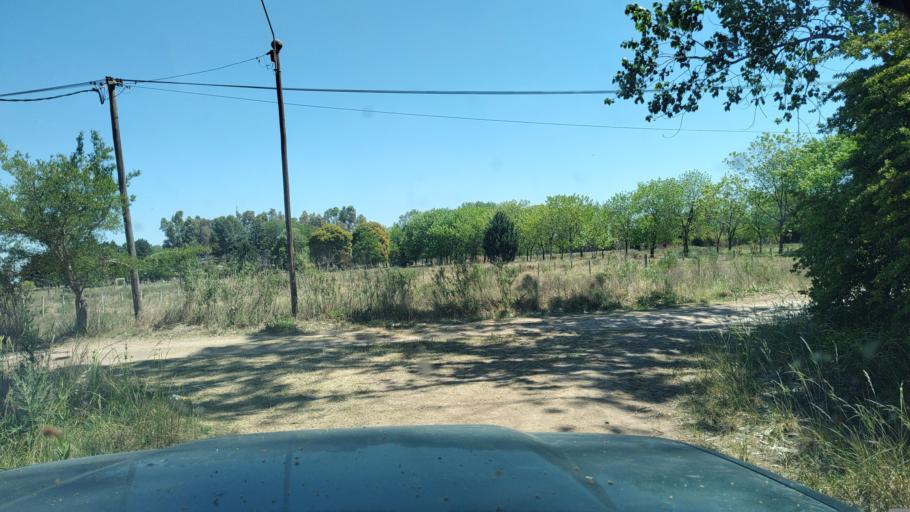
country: AR
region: Buenos Aires
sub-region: Partido de Lujan
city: Lujan
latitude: -34.6007
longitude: -59.1405
